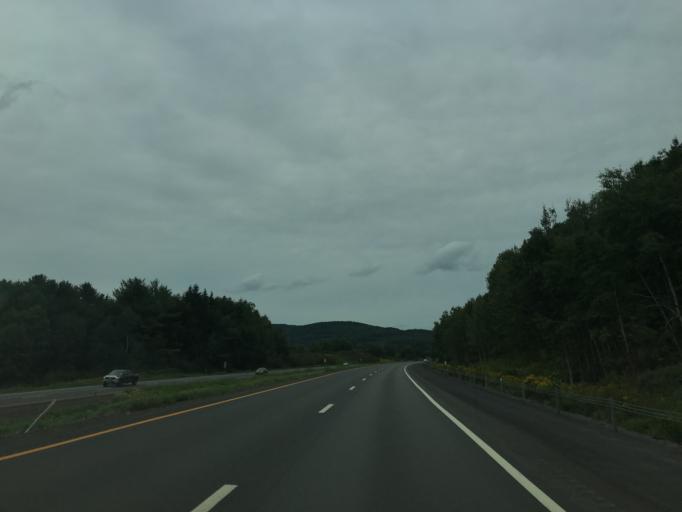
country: US
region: New York
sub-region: Delaware County
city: Sidney
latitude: 42.3116
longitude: -75.3548
